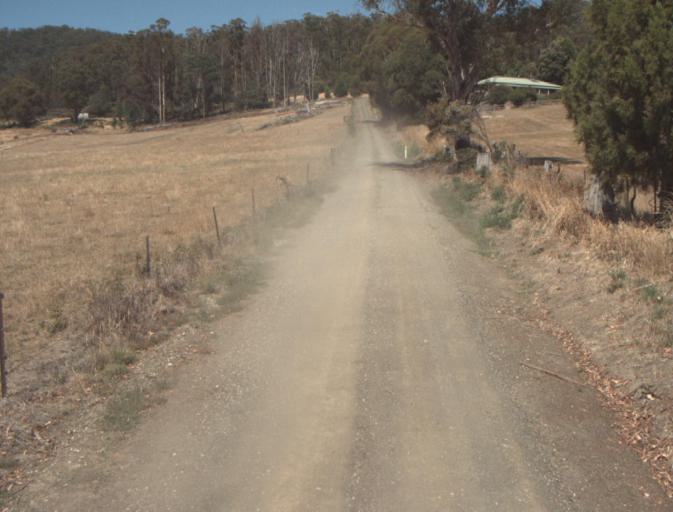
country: AU
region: Tasmania
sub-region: Launceston
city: Mayfield
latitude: -41.2639
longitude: 147.1493
